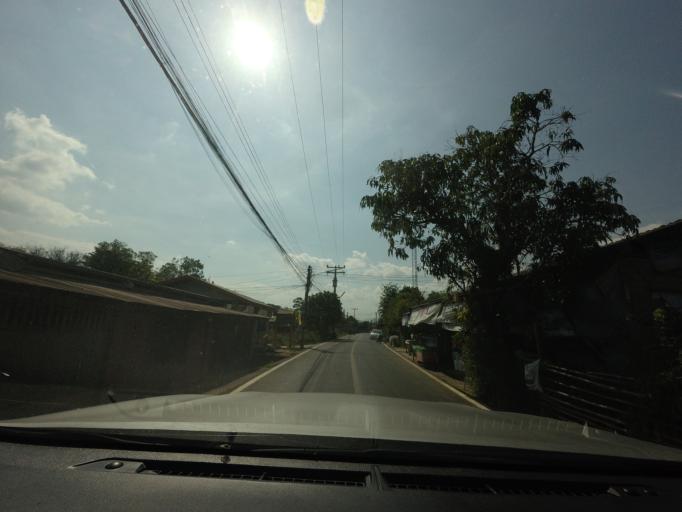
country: TH
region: Mae Hong Son
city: Wiang Nuea
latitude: 19.3853
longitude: 98.4396
